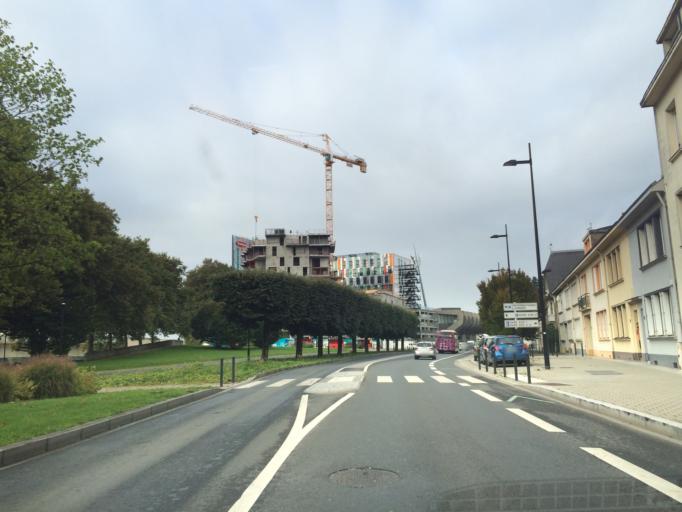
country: FR
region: Pays de la Loire
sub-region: Departement de la Loire-Atlantique
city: Nantes
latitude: 47.2132
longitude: -1.5346
